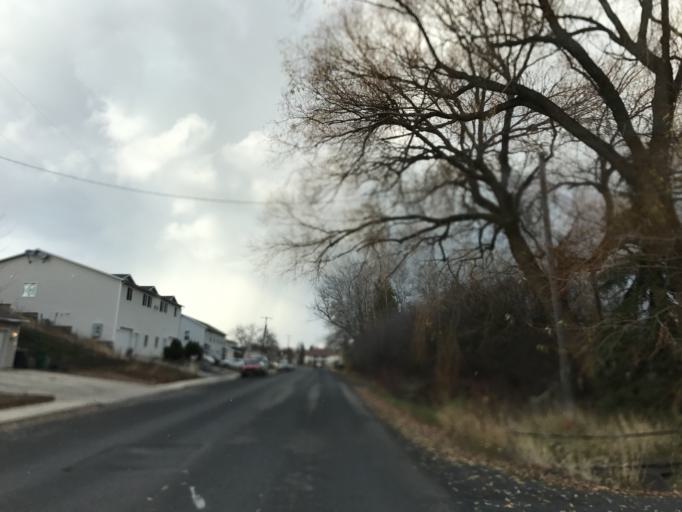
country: US
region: Idaho
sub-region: Latah County
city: Moscow
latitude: 46.7428
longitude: -116.9941
